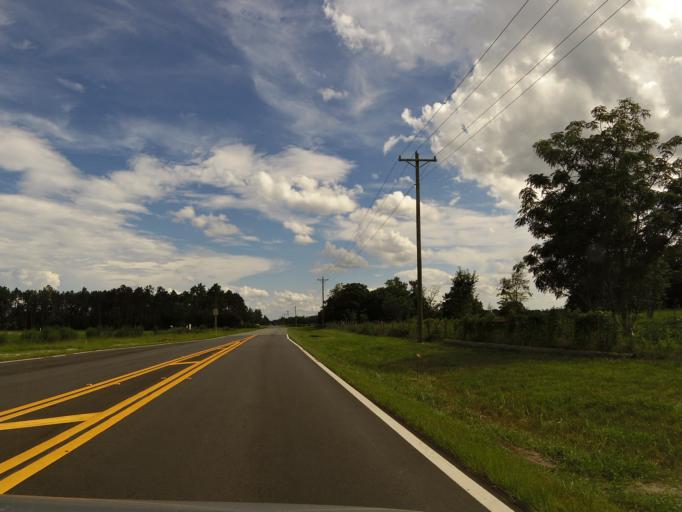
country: US
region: Florida
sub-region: Clay County
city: Green Cove Springs
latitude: 30.0143
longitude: -81.7316
